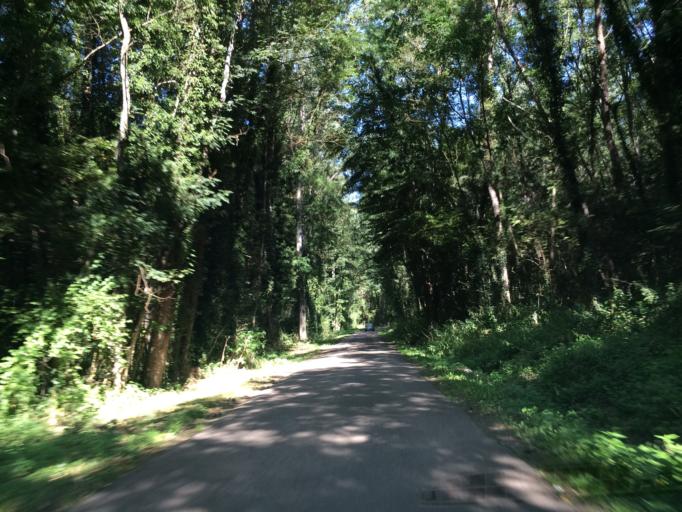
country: FR
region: Bourgogne
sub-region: Departement de l'Yonne
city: Fleury-la-Vallee
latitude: 47.8545
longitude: 3.3990
